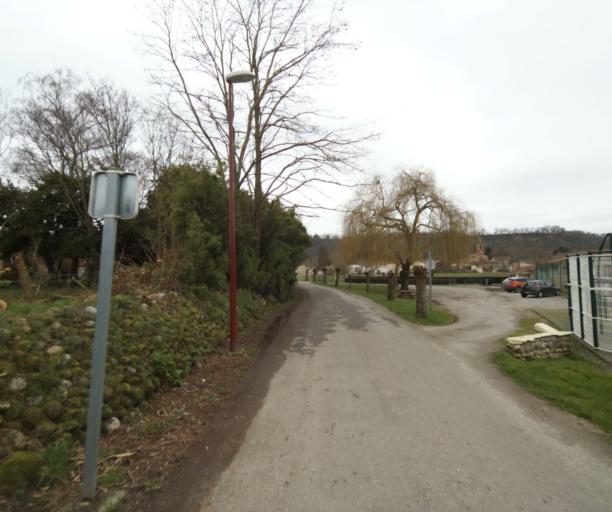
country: FR
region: Midi-Pyrenees
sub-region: Departement de l'Ariege
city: Saverdun
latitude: 43.1840
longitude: 1.6052
